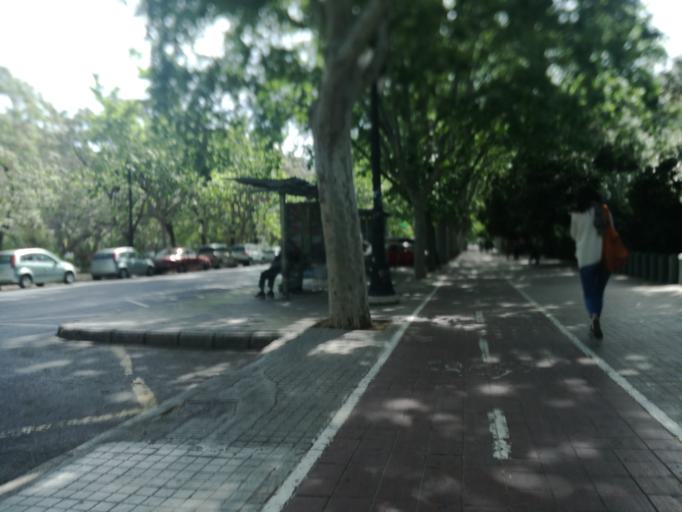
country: ES
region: Valencia
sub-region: Provincia de Valencia
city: Valencia
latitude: 39.4776
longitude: -0.3617
